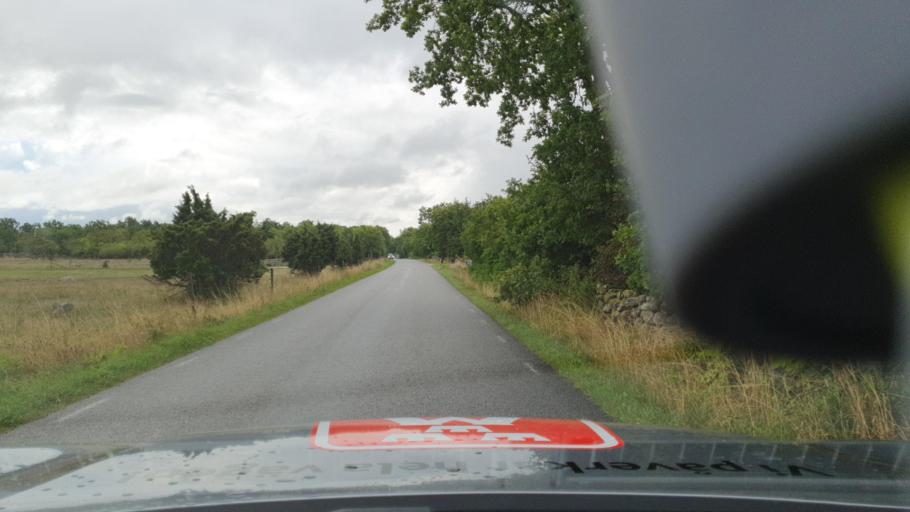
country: SE
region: Gotland
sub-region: Gotland
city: Hemse
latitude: 57.0707
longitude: 18.3141
